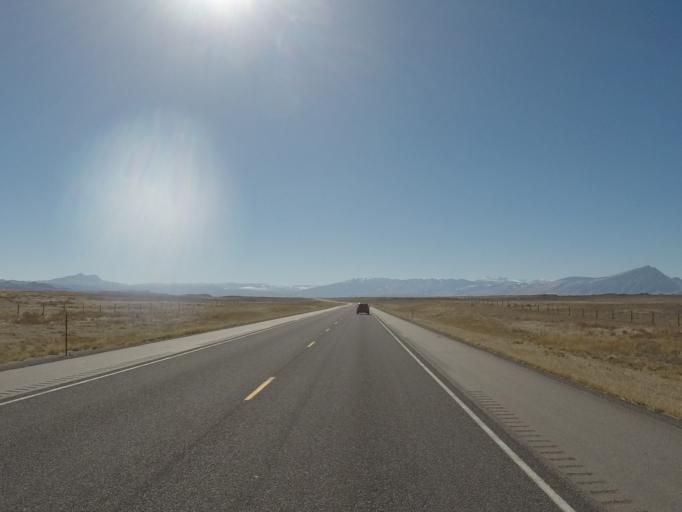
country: US
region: Montana
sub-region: Carbon County
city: Red Lodge
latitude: 44.9231
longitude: -109.0899
